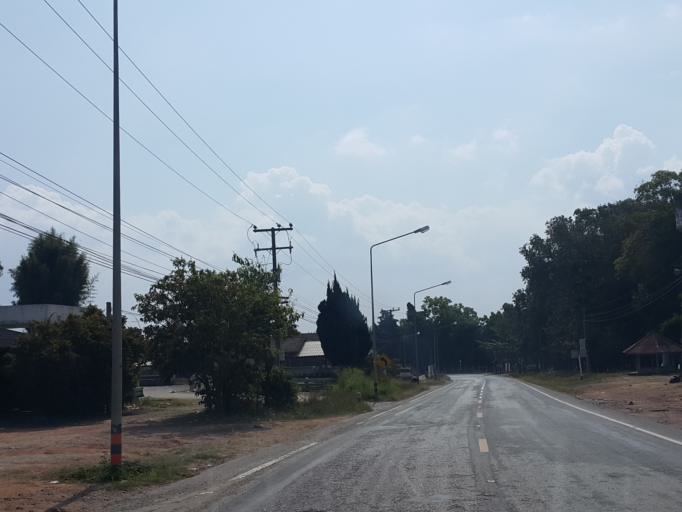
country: TH
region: Chiang Mai
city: Hot
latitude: 18.1071
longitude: 98.3746
